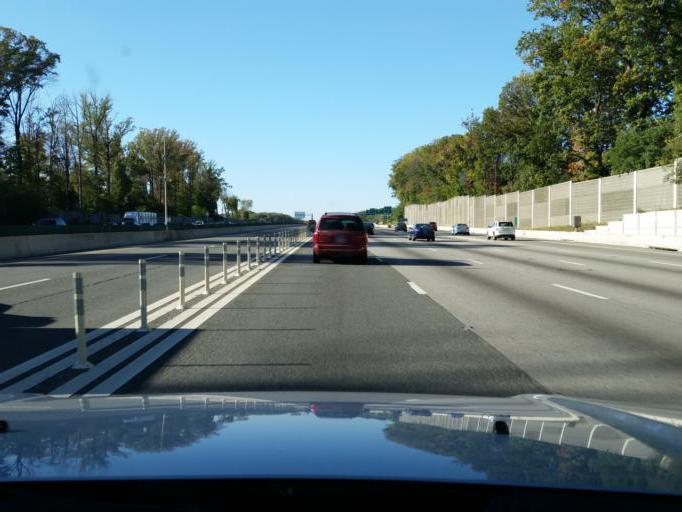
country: US
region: Virginia
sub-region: Fairfax County
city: Ravensworth
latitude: 38.8052
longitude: -77.2131
